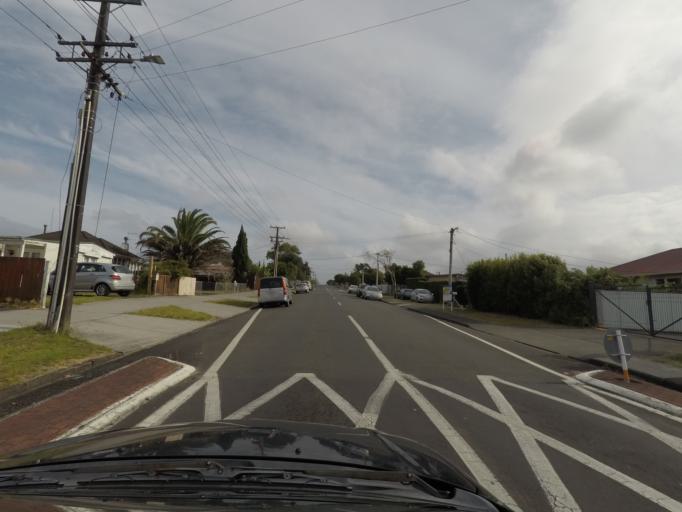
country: NZ
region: Auckland
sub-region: Auckland
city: Waitakere
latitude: -36.9017
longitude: 174.6659
